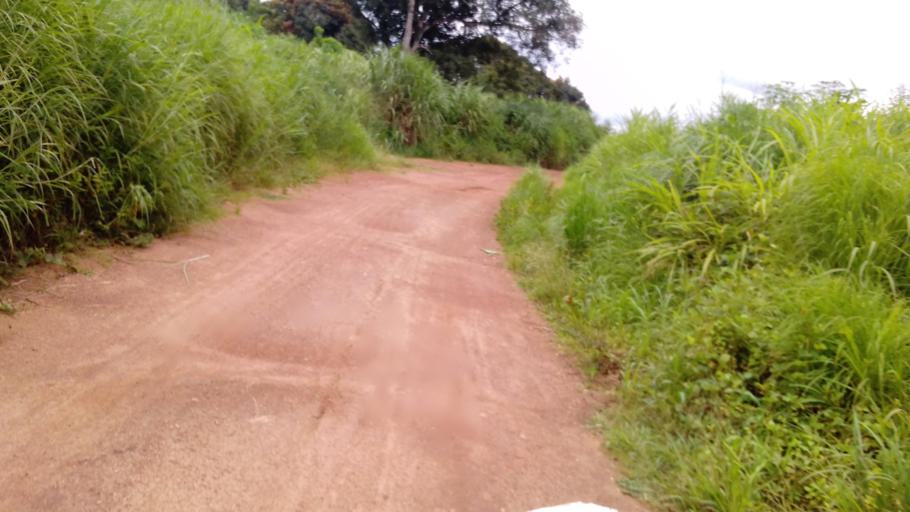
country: SL
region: Eastern Province
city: Koidu
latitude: 8.6634
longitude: -10.9418
